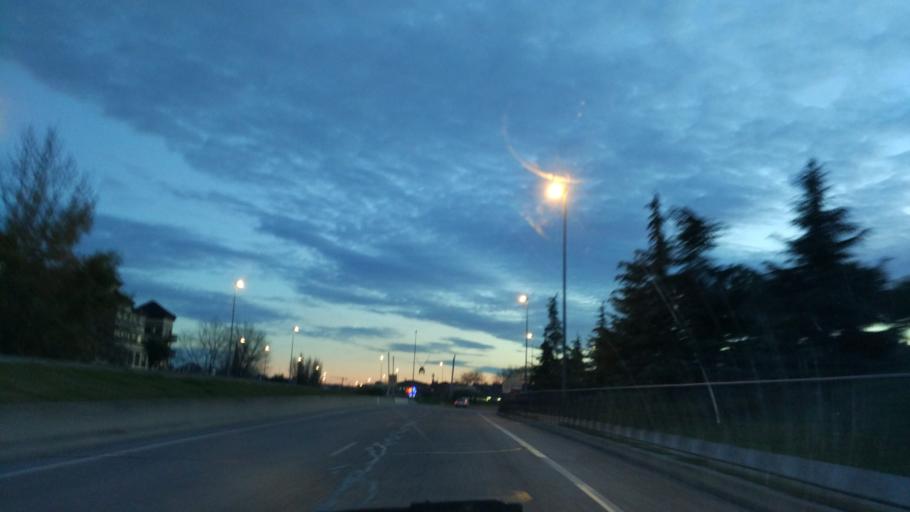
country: ES
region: Madrid
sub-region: Provincia de Madrid
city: Leganes
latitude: 40.3404
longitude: -3.7706
